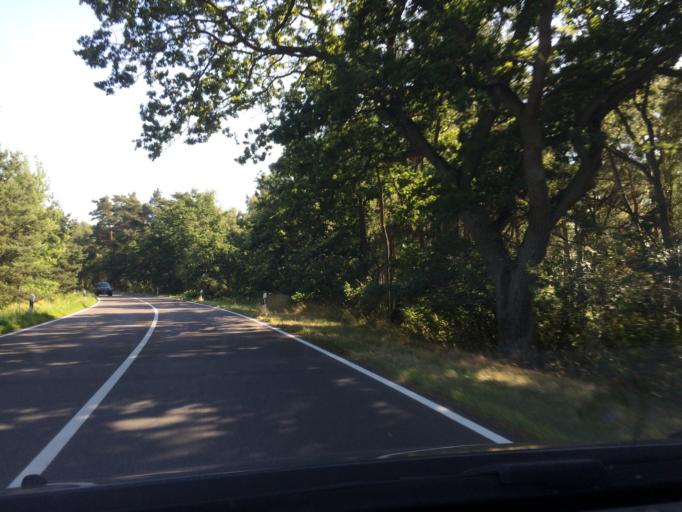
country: DE
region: Mecklenburg-Vorpommern
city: Zingst
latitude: 54.4229
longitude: 12.6511
